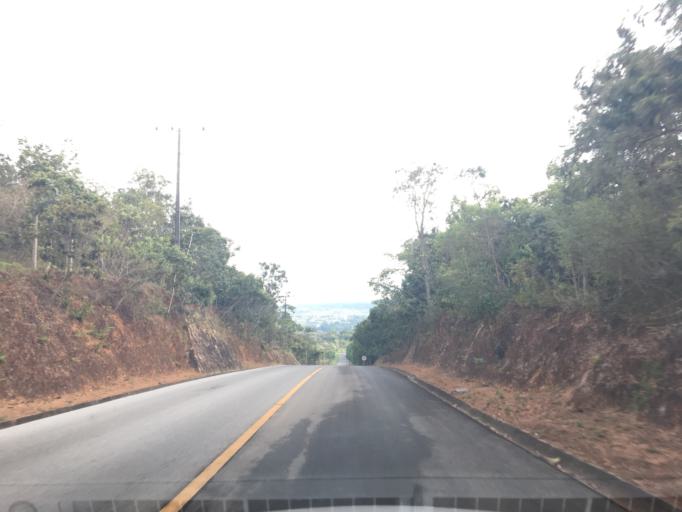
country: BR
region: Federal District
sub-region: Brasilia
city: Brasilia
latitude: -15.8023
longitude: -47.7995
